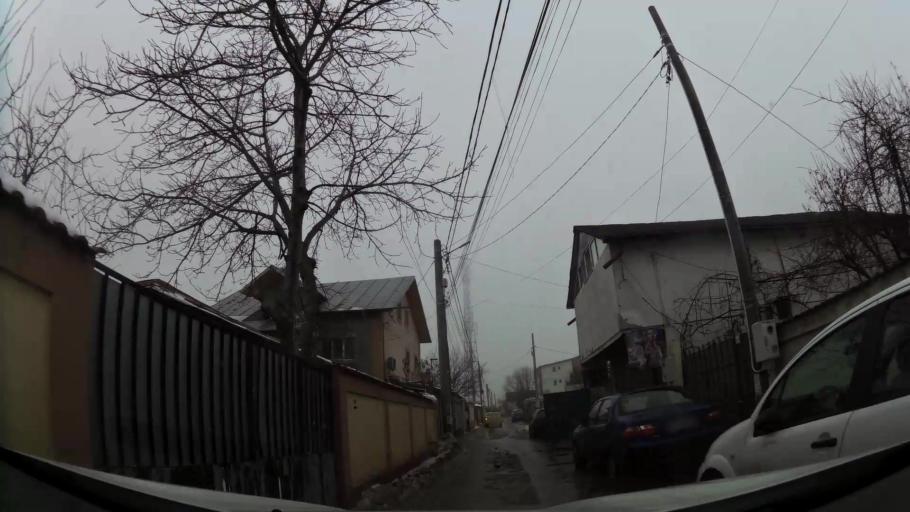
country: RO
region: Ilfov
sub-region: Comuna Chiajna
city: Rosu
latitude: 44.4470
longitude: 26.0115
